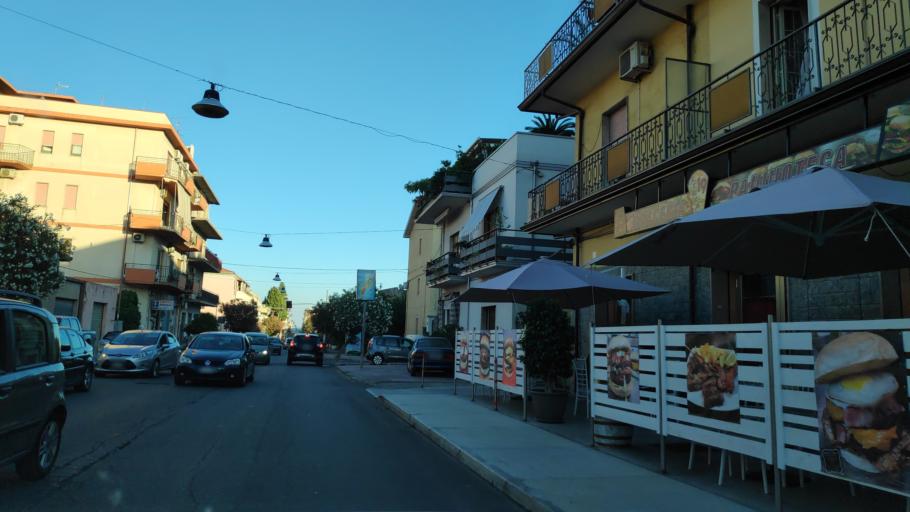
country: IT
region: Calabria
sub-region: Provincia di Reggio Calabria
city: Locri
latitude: 38.2372
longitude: 16.2580
